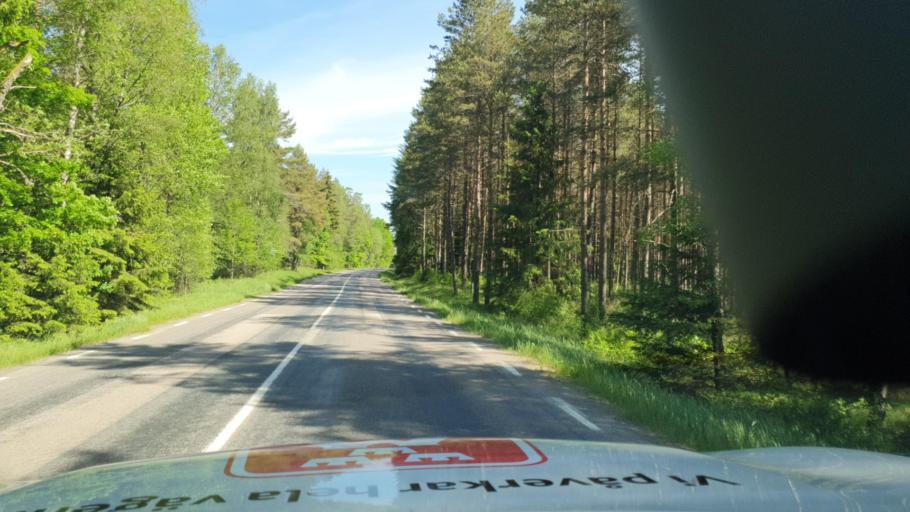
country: SE
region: Vaestra Goetaland
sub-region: Herrljunga Kommun
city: Herrljunga
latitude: 57.9810
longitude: 13.0816
